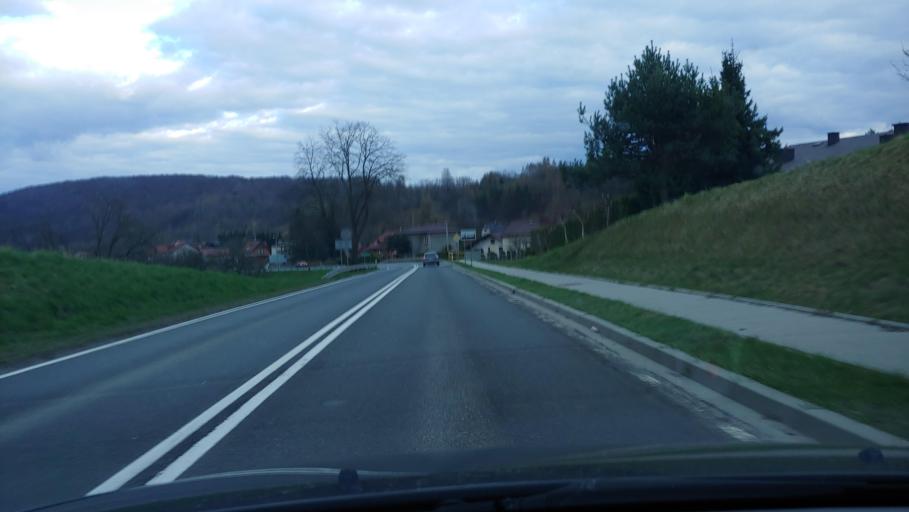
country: PL
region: Lesser Poland Voivodeship
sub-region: Powiat krakowski
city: Rudawa
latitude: 50.1155
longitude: 19.6978
